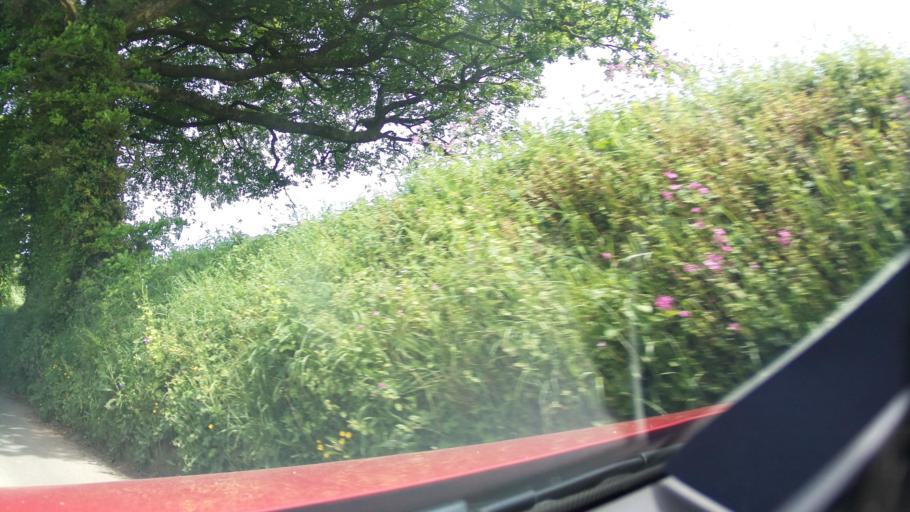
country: GB
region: England
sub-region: Devon
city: Totnes
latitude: 50.3636
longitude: -3.7282
